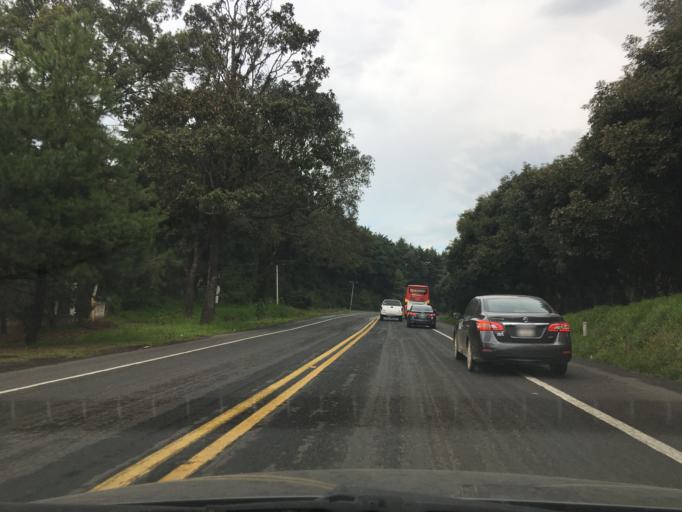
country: MX
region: Michoacan
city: Capacuaro
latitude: 19.5206
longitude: -102.0778
